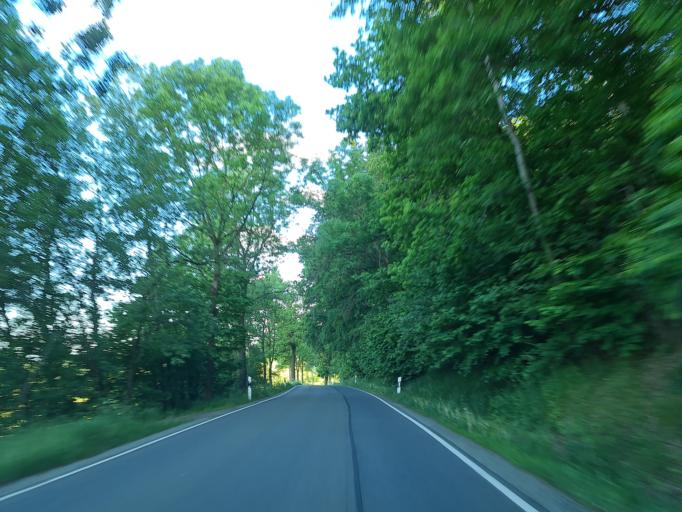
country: DE
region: Saxony
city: Reuth
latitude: 50.4695
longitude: 11.9924
